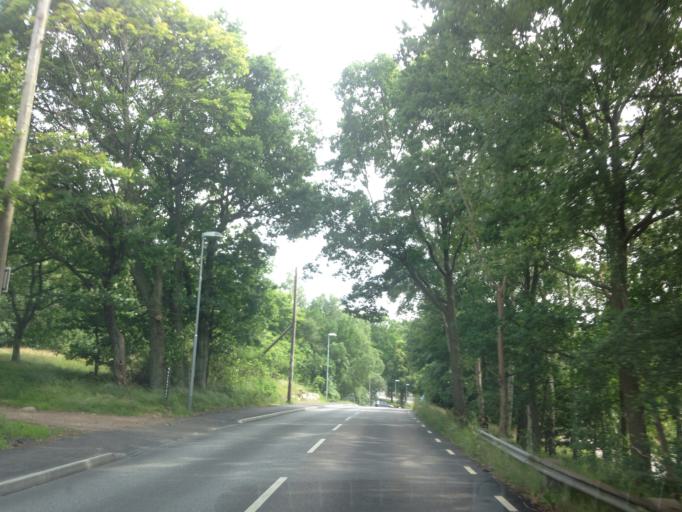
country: SE
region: Vaestra Goetaland
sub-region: Goteborg
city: Goeteborg
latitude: 57.7629
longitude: 11.9499
